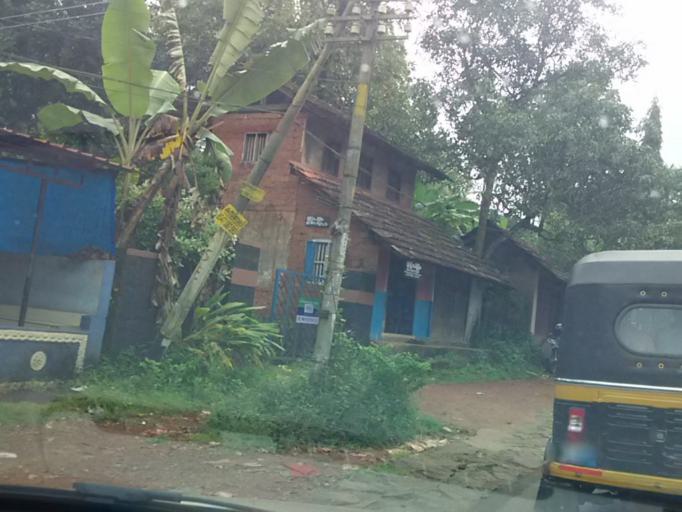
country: IN
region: Kerala
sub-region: Kozhikode
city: Kunnamangalam
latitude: 11.3084
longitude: 75.9038
